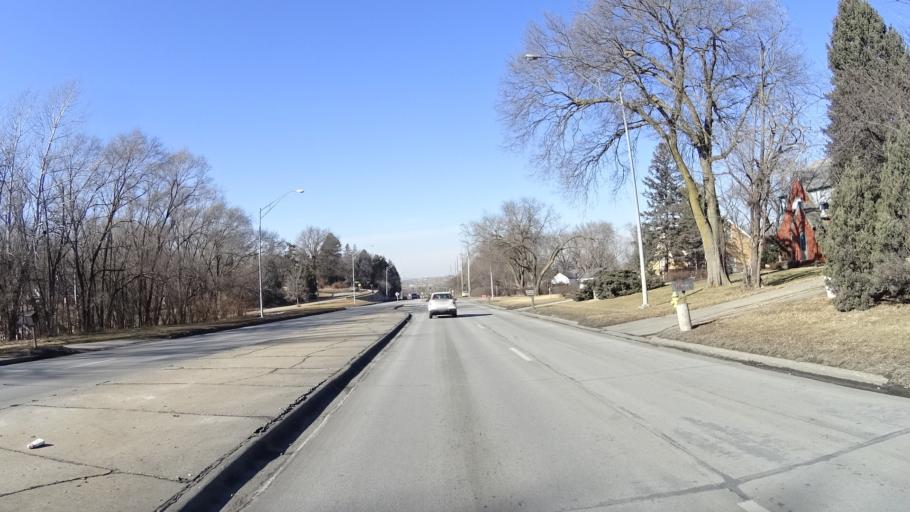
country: US
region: Nebraska
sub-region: Douglas County
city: Ralston
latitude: 41.3043
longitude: -96.0352
